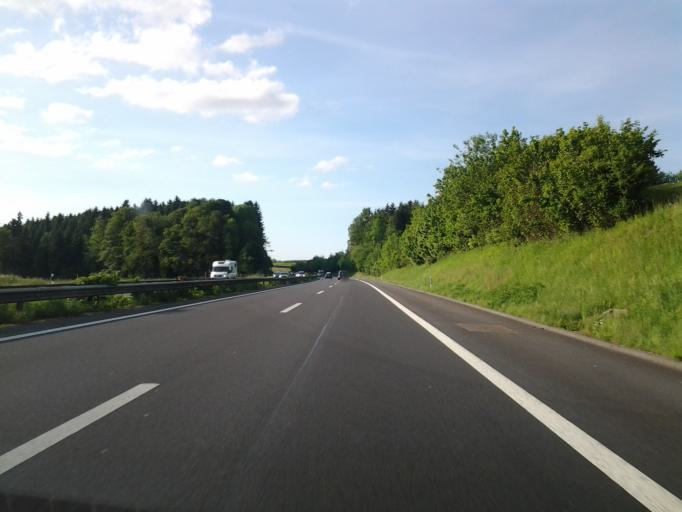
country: CH
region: Lucerne
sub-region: Hochdorf District
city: Emmen
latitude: 47.0981
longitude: 8.2458
